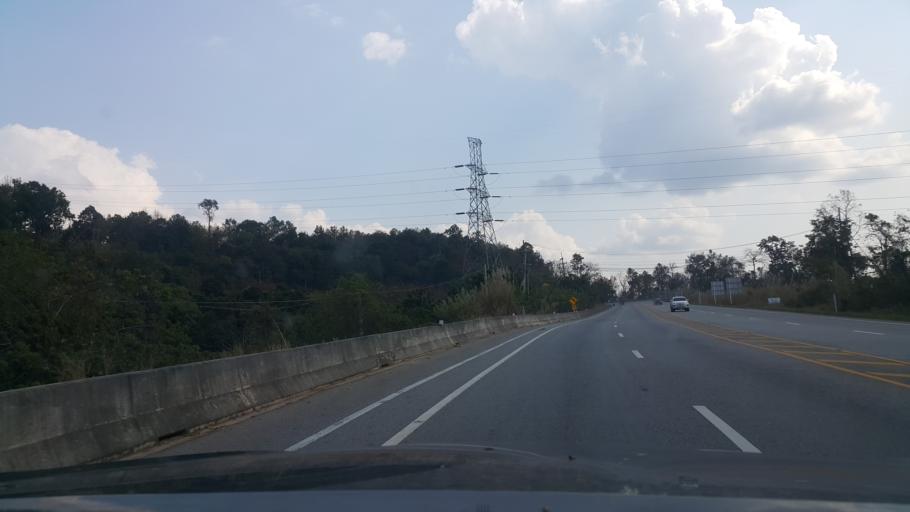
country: TH
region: Phitsanulok
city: Nakhon Thai
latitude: 16.8847
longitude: 100.8121
